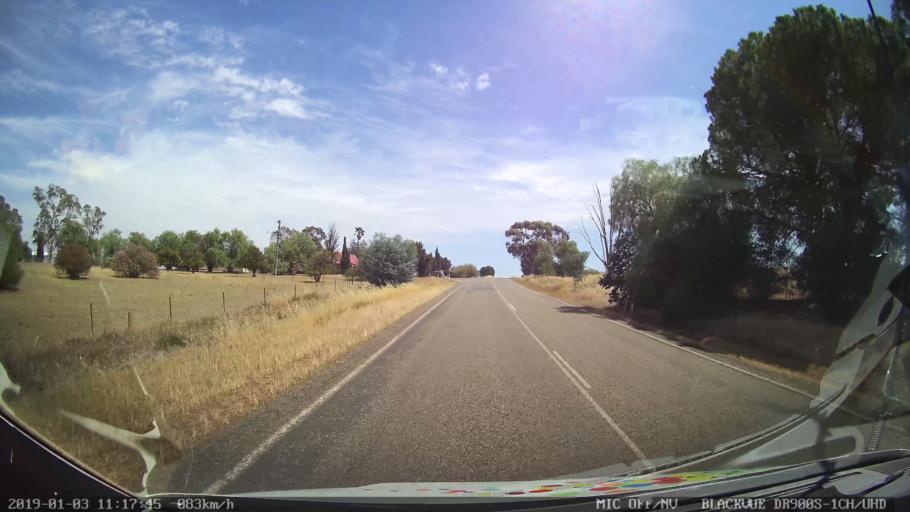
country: AU
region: New South Wales
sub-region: Young
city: Young
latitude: -34.1348
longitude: 148.2646
